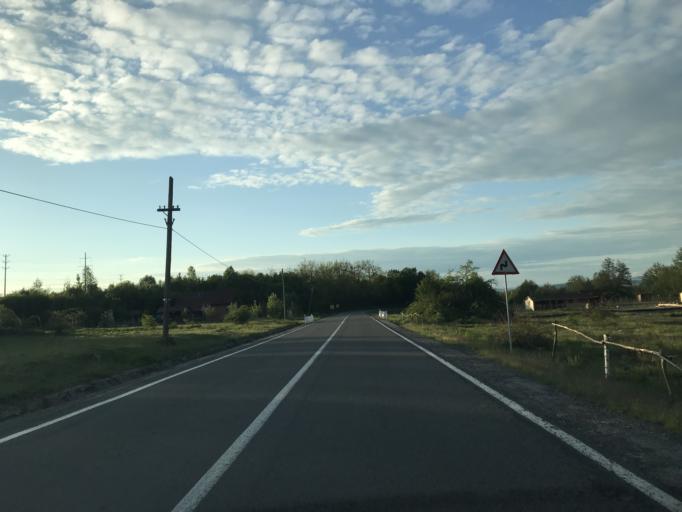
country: RO
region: Sibiu
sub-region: Comuna Cartisoara
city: Cartisoara
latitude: 45.6984
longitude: 24.5707
